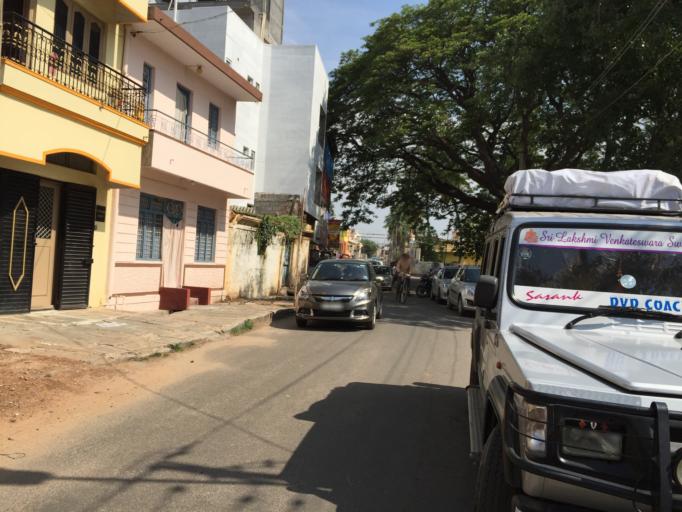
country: IN
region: Karnataka
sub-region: Mysore
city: Mysore
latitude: 12.3044
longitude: 76.6615
